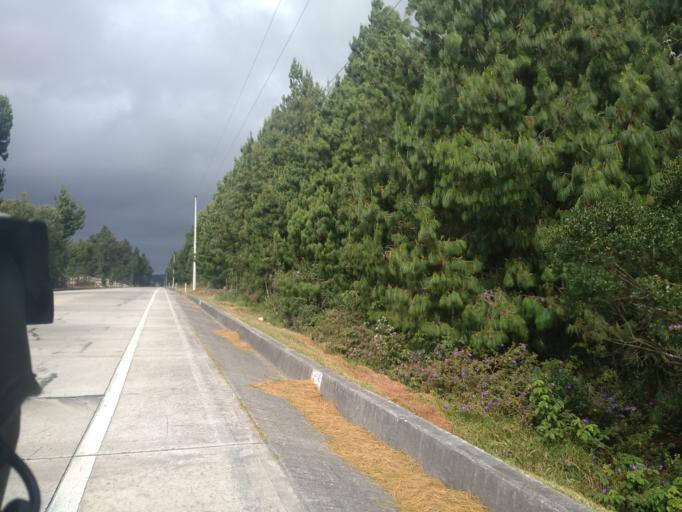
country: EC
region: Azuay
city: Cuenca
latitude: -3.3491
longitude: -79.1839
